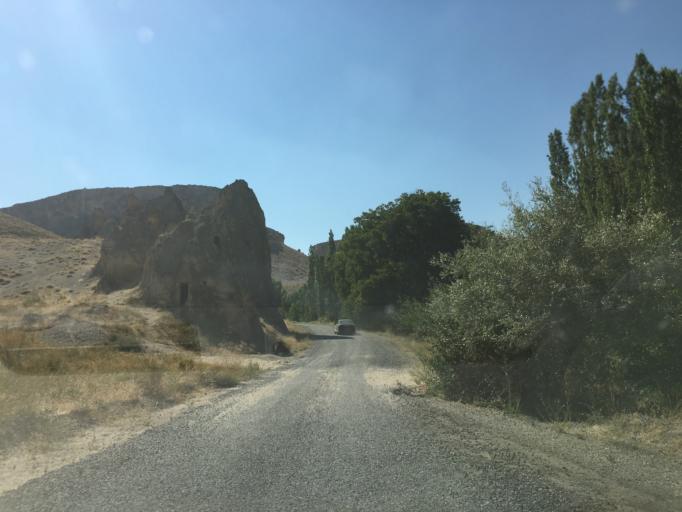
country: TR
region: Kayseri
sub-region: Yesilhisar
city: Yesilhisar
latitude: 38.3449
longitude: 34.9669
